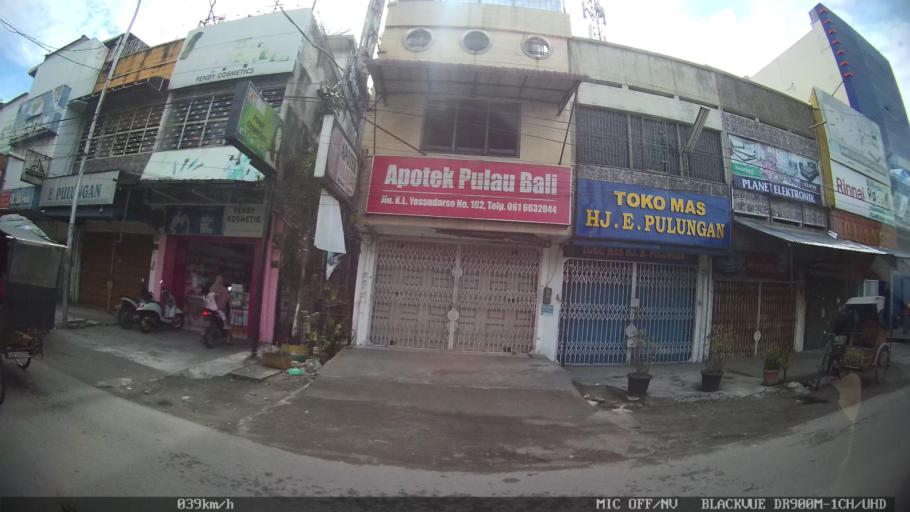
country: ID
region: North Sumatra
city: Medan
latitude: 3.6262
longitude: 98.6692
